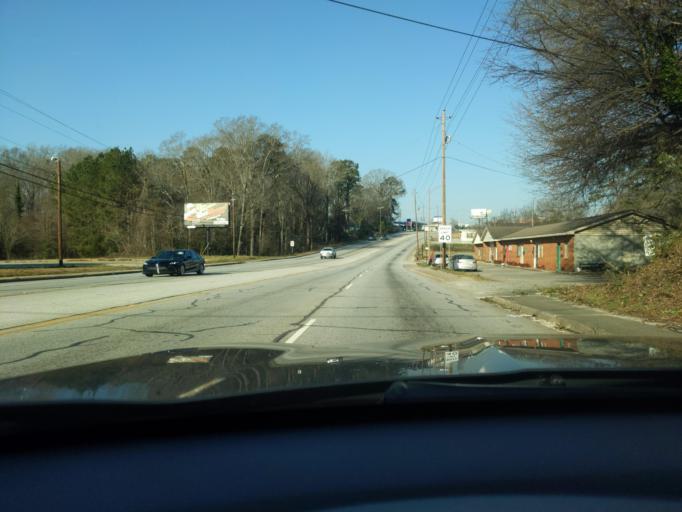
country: US
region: South Carolina
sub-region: Greenwood County
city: Greenwood
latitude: 34.2071
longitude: -82.1417
